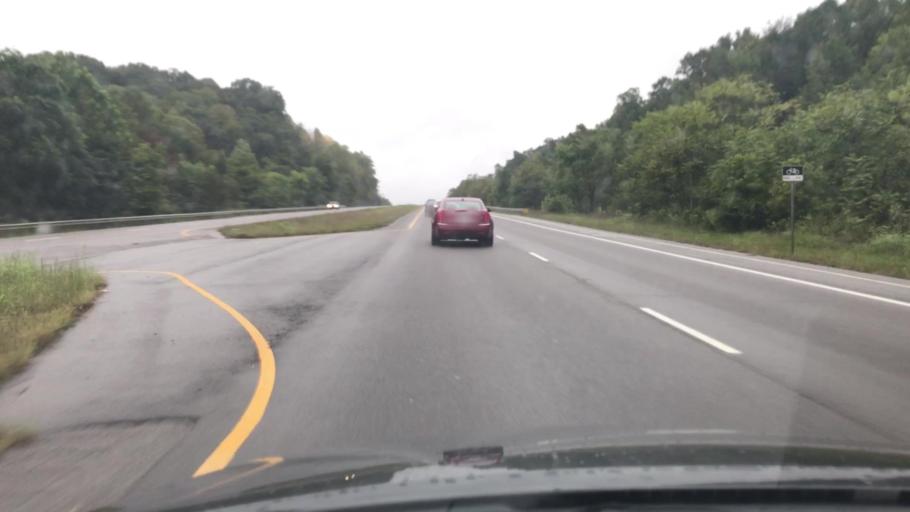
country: US
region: Tennessee
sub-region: Cheatham County
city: Ashland City
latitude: 36.2111
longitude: -86.9562
